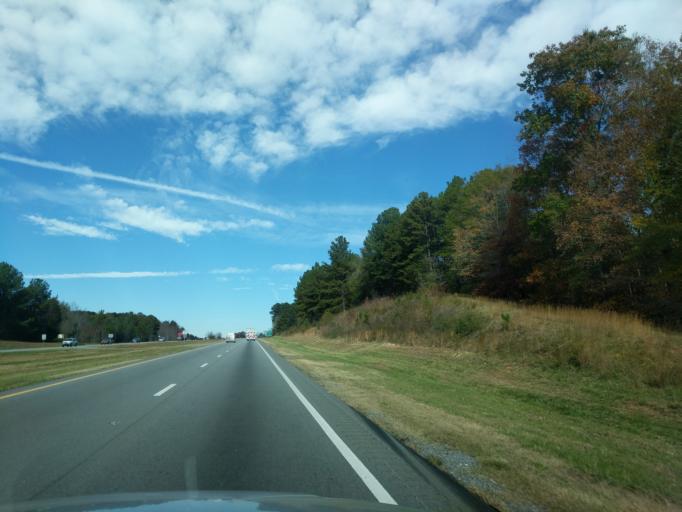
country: US
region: North Carolina
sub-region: Lincoln County
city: Lincolnton
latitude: 35.4053
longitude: -81.2099
